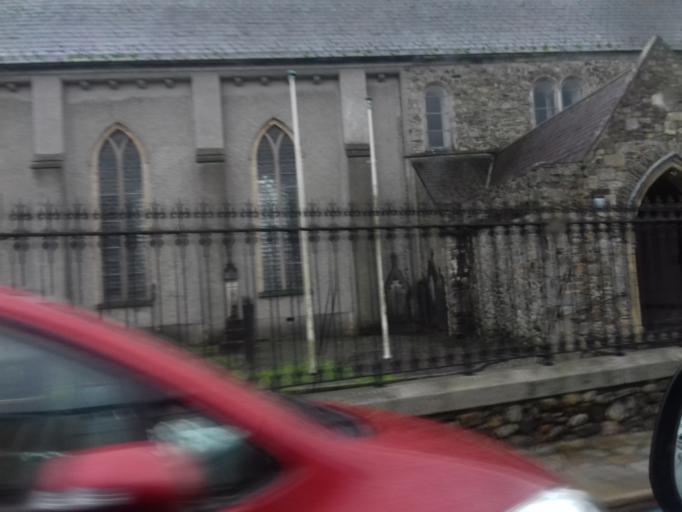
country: IE
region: Leinster
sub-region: Kilkenny
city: Graiguenamanagh
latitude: 52.5414
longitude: -6.9550
